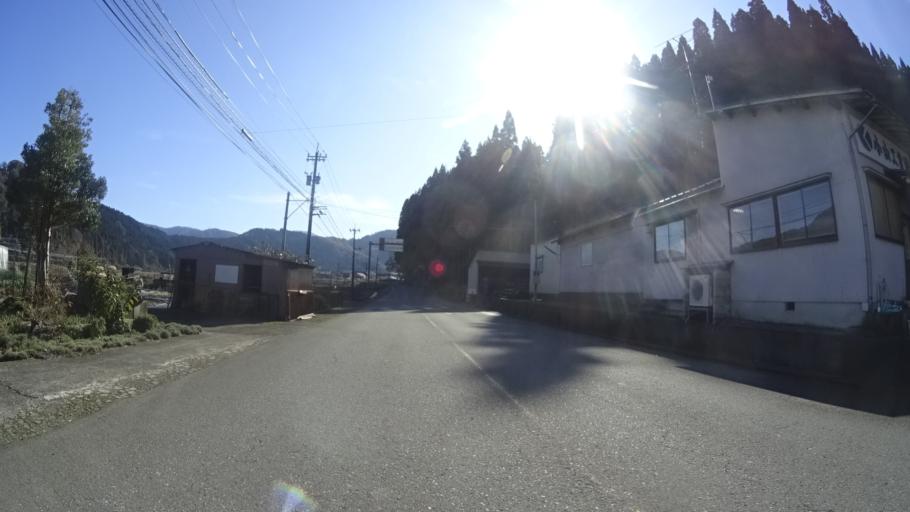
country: JP
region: Ishikawa
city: Tsurugi-asahimachi
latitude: 36.3633
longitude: 136.5936
